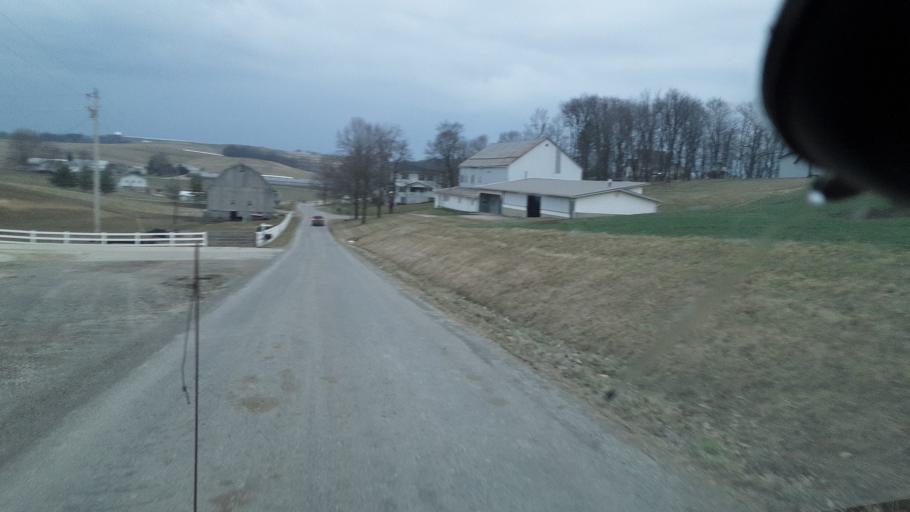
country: US
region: Ohio
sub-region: Tuscarawas County
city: Sugarcreek
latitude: 40.4992
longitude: -81.6800
